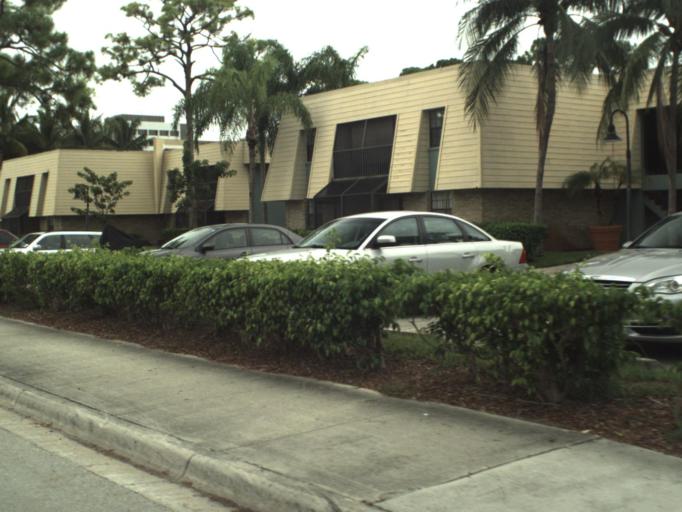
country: US
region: Florida
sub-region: Palm Beach County
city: North Palm Beach
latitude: 26.8347
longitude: -80.1052
